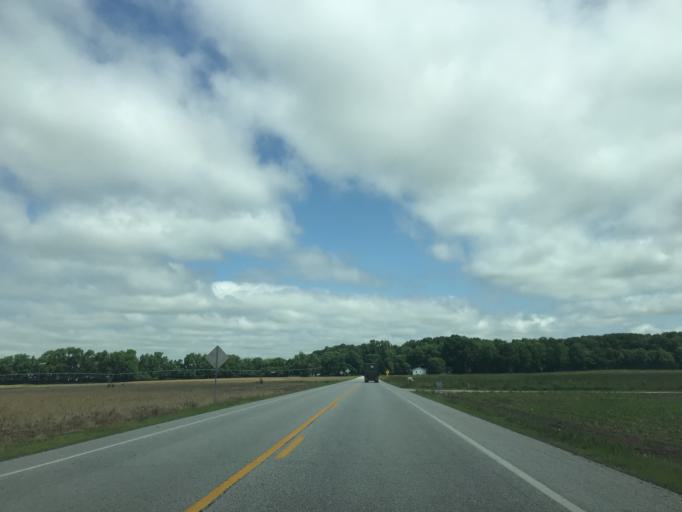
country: US
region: Maryland
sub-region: Caroline County
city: Ridgely
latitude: 38.9172
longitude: -75.8933
